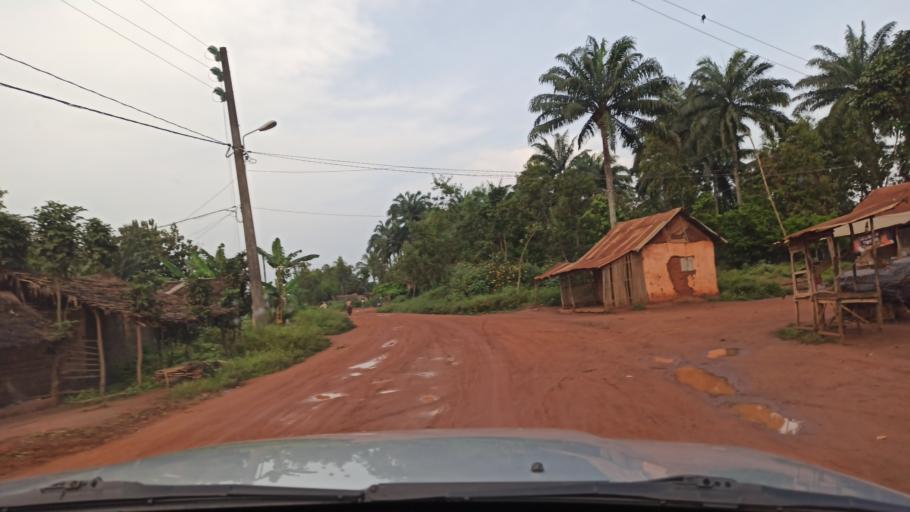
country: BJ
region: Queme
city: Porto-Novo
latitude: 6.4975
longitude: 2.6975
